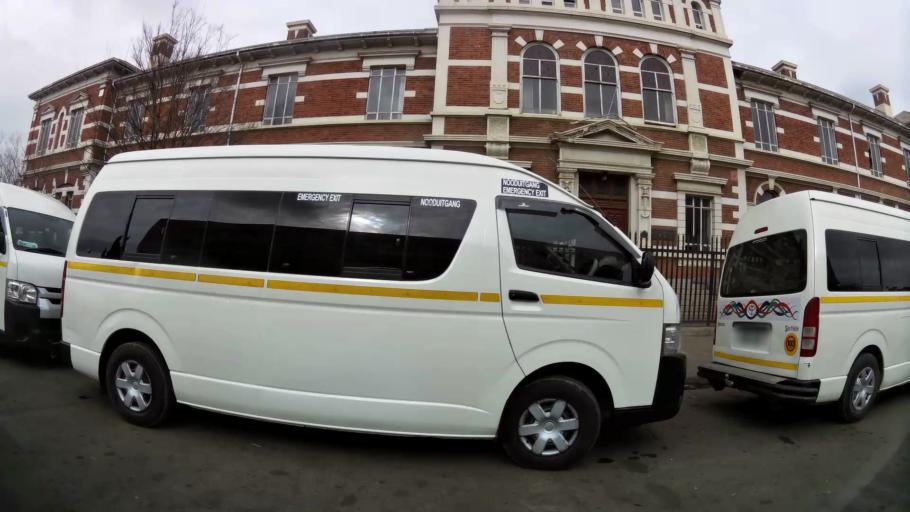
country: ZA
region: Orange Free State
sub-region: Mangaung Metropolitan Municipality
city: Bloemfontein
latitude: -29.1186
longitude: 26.2254
